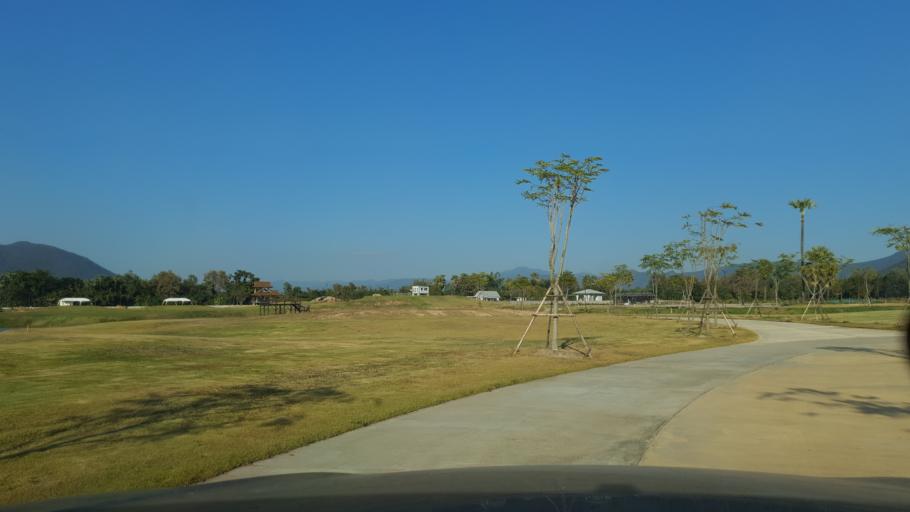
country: TH
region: Chiang Mai
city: Mae On
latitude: 18.7232
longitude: 99.2136
